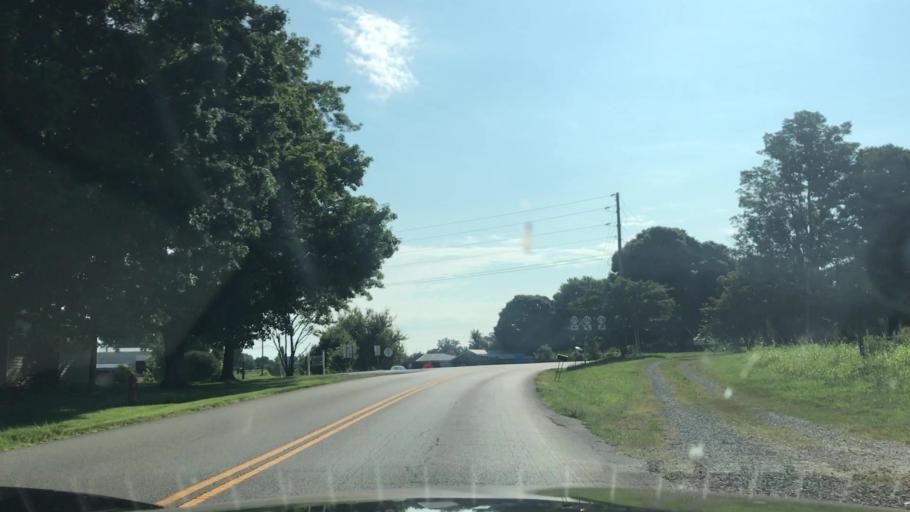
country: US
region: Kentucky
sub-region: Hart County
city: Horse Cave
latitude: 37.1781
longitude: -85.7833
